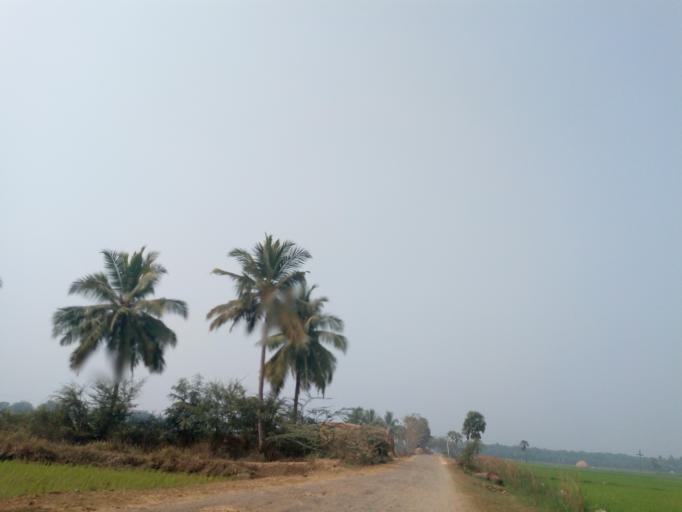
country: IN
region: Andhra Pradesh
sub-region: West Godavari
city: Tadepallegudem
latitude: 16.8640
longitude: 81.3113
